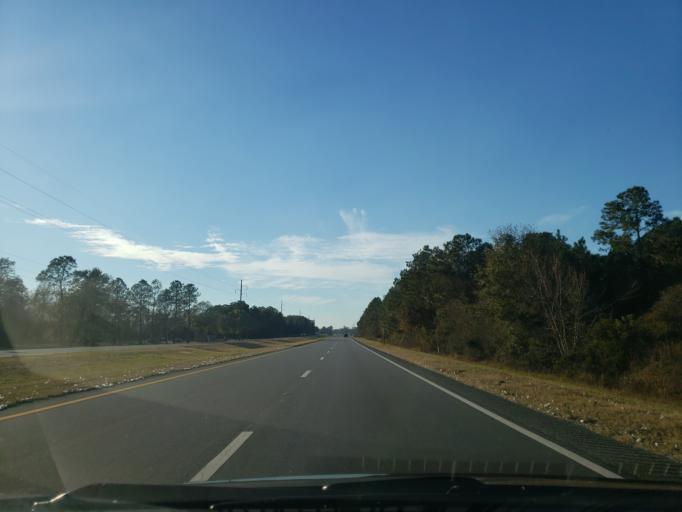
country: US
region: Georgia
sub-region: Atkinson County
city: Pearson
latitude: 31.2941
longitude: -82.8286
